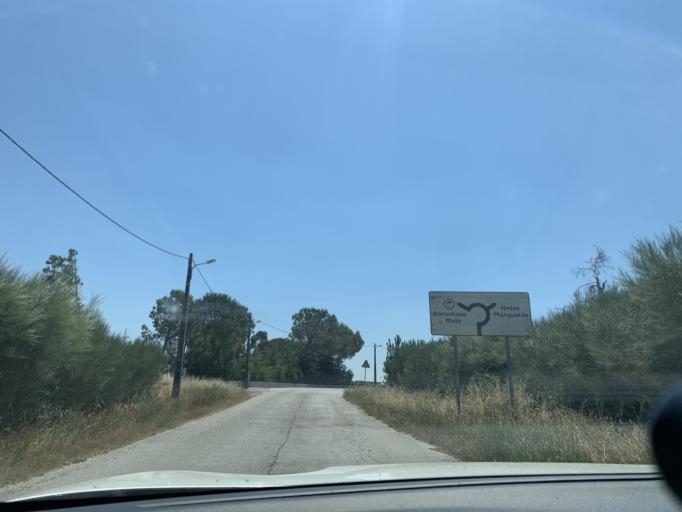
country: PT
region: Viseu
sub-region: Mangualde
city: Mangualde
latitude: 40.5485
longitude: -7.7398
